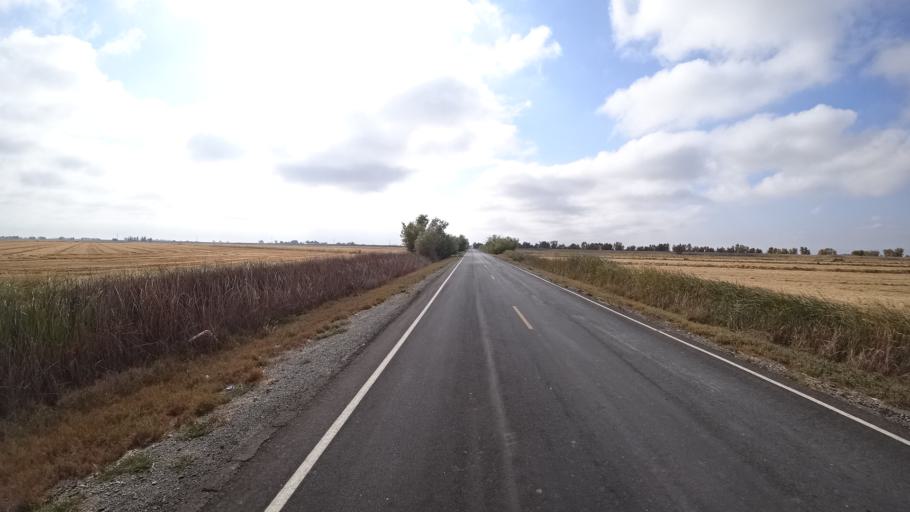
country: US
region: California
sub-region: Yolo County
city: Woodland
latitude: 38.8096
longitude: -121.7743
